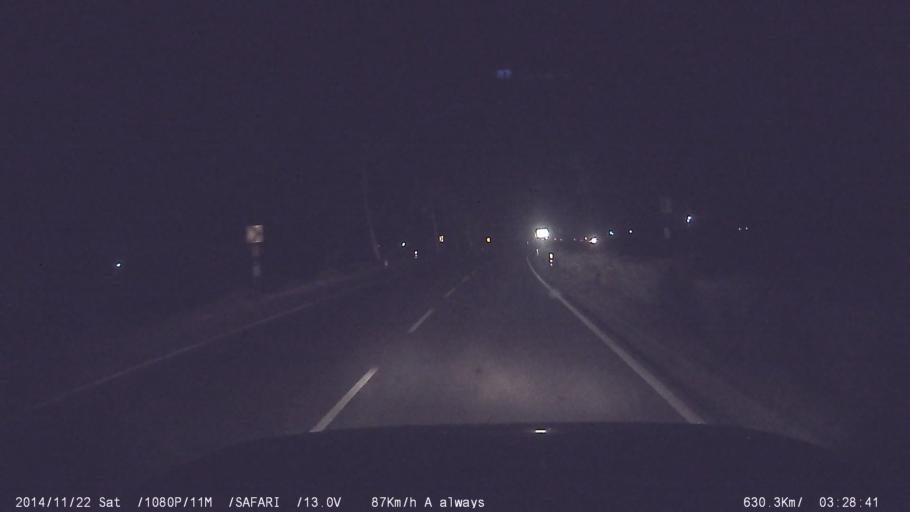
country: IN
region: Tamil Nadu
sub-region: Salem
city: Konganapuram
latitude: 11.5224
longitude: 77.9415
